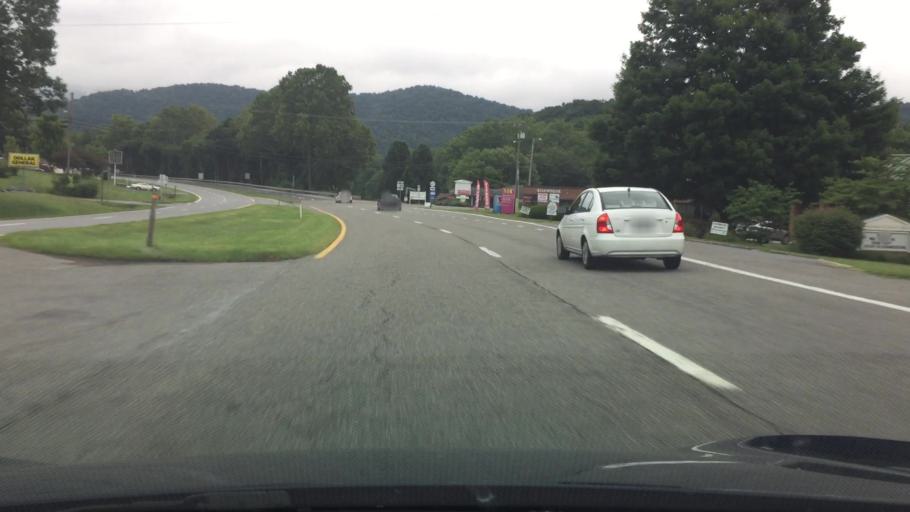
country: US
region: Virginia
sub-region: Montgomery County
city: Shawsville
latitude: 37.1678
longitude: -80.2570
